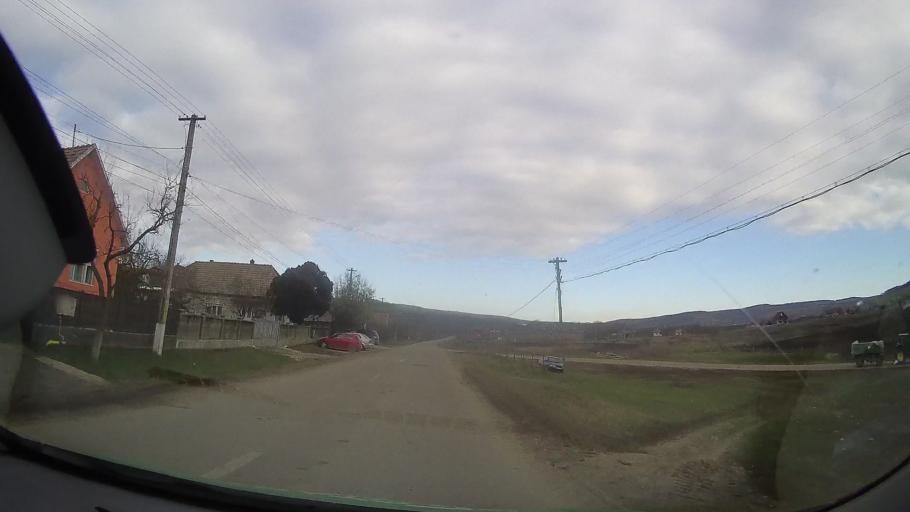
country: RO
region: Mures
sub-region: Comuna Iernut
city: Iernut
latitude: 46.4801
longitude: 24.2290
